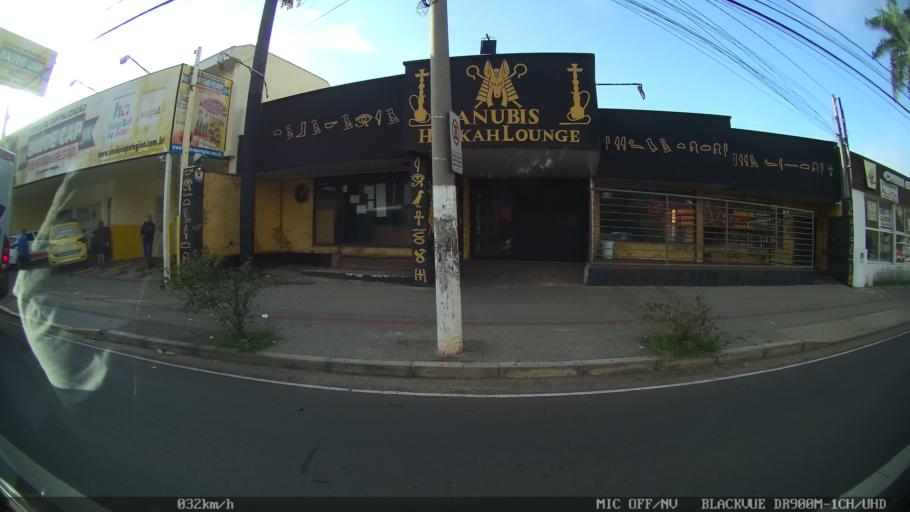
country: BR
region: Sao Paulo
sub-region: Sao Jose Do Rio Preto
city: Sao Jose do Rio Preto
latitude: -20.8191
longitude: -49.3825
